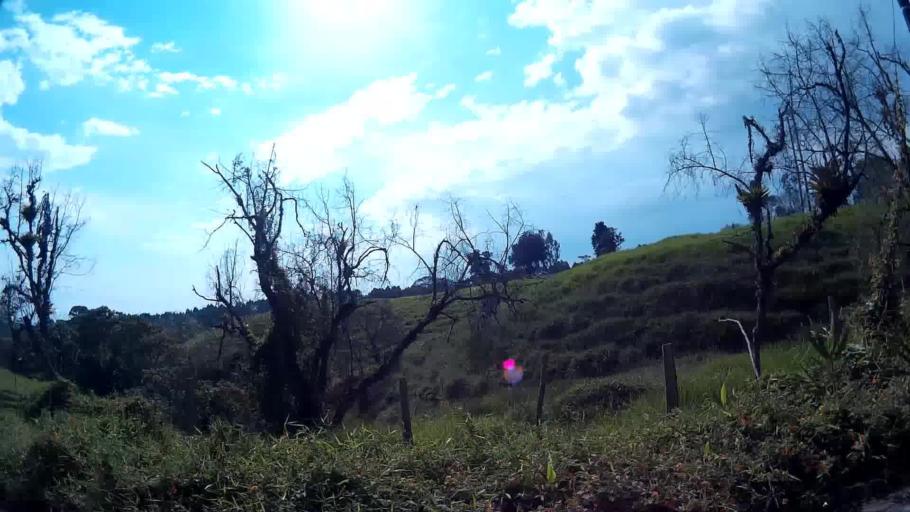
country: CO
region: Quindio
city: Filandia
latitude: 4.6864
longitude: -75.6346
